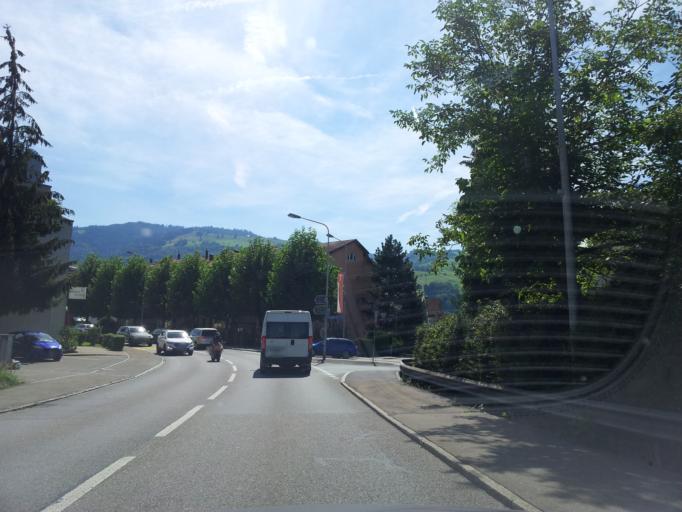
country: CH
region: Schwyz
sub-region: Bezirk March
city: Lachen
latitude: 47.1896
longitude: 8.8574
